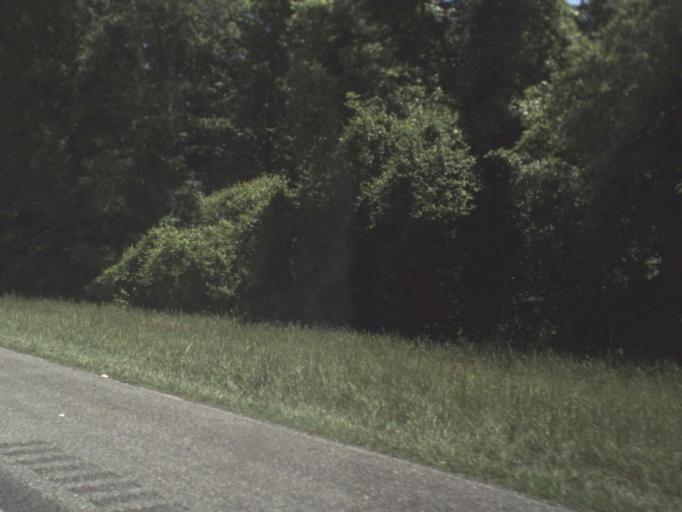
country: US
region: Florida
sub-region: Jefferson County
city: Monticello
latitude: 30.4894
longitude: -83.9938
